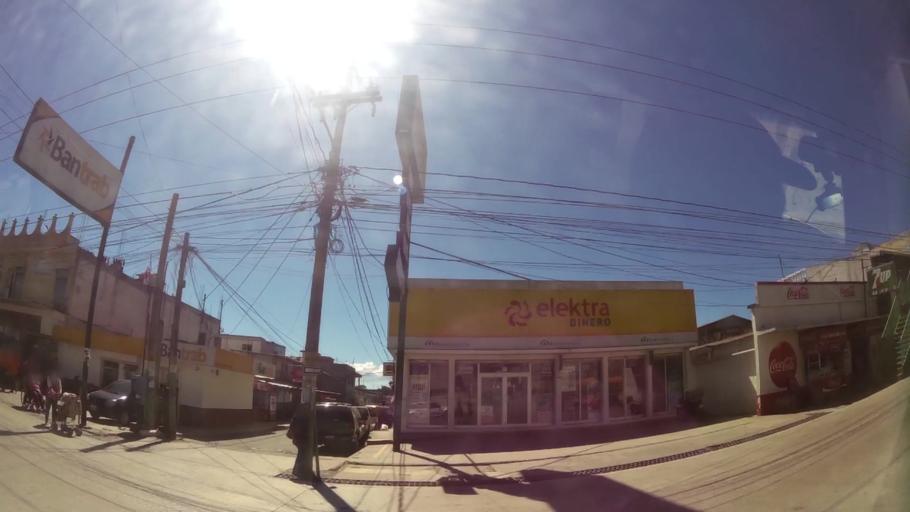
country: GT
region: Guatemala
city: San Jose Pinula
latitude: 14.5460
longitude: -90.4123
